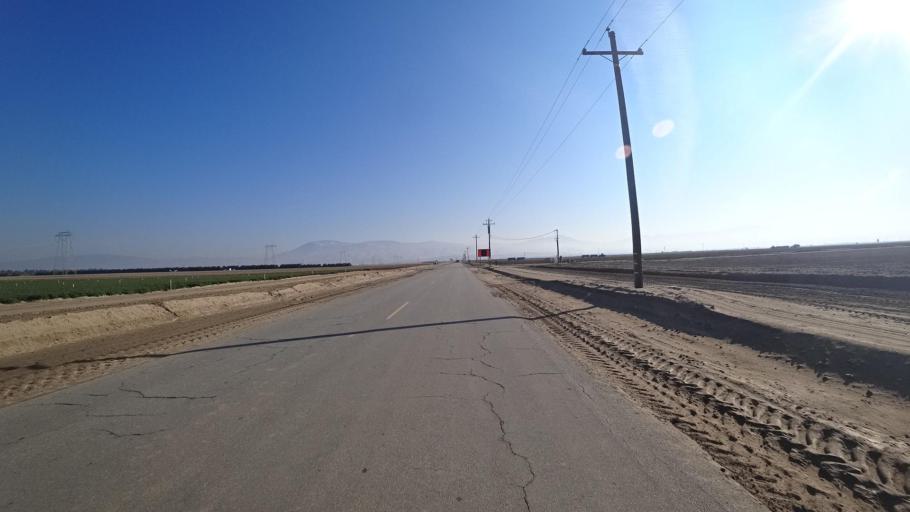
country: US
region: California
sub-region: Kern County
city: Weedpatch
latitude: 35.1220
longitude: -118.9202
